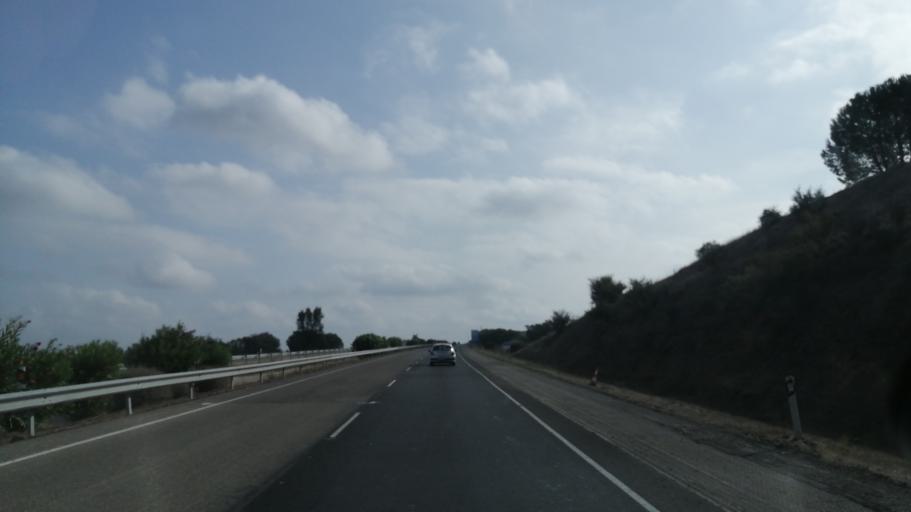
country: PT
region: Evora
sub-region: Vendas Novas
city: Vendas Novas
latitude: 38.6415
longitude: -8.4641
